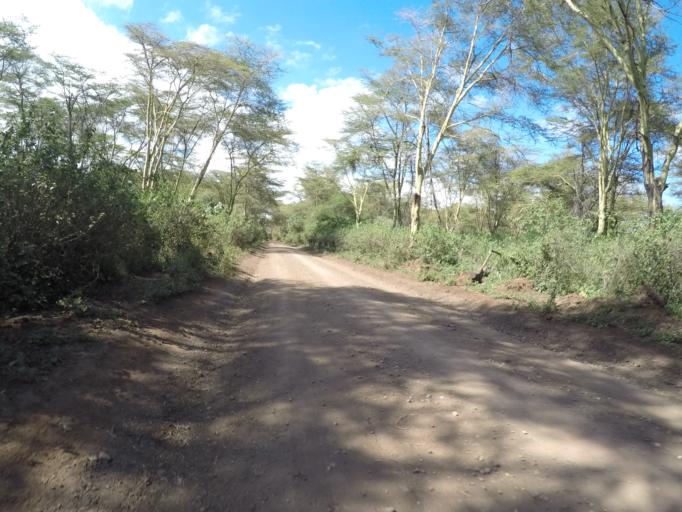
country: TZ
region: Arusha
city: Mto wa Mbu
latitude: -3.4047
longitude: 35.8246
